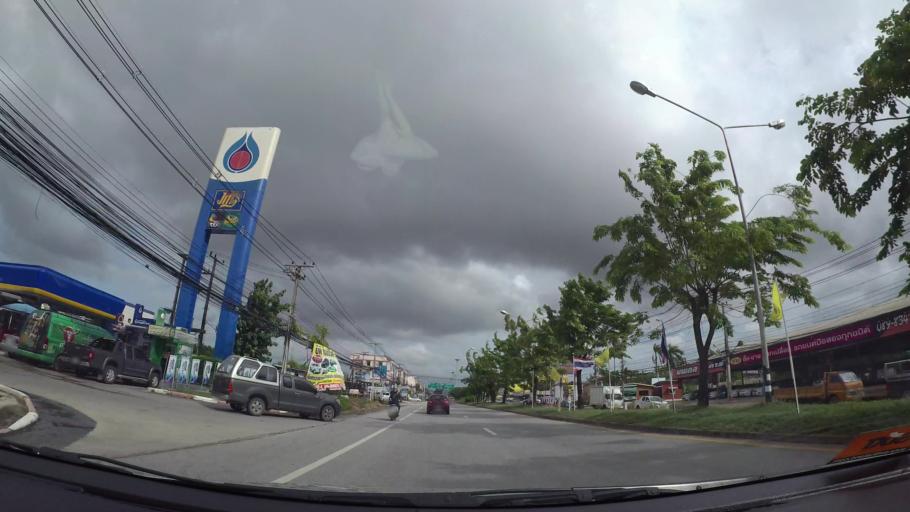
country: TH
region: Rayong
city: Rayong
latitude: 12.6882
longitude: 101.2105
